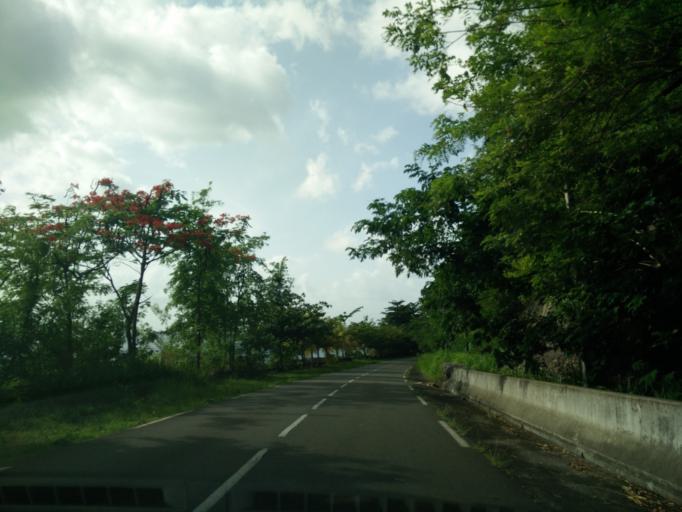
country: MQ
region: Martinique
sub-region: Martinique
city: Saint-Pierre
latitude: 14.8123
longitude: -61.2285
